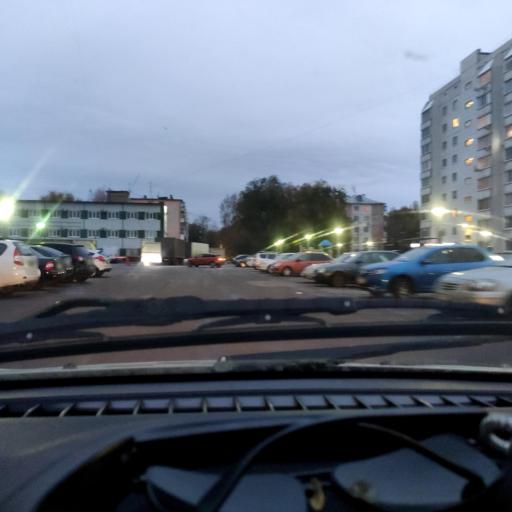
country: RU
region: Samara
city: Tol'yatti
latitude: 53.5197
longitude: 49.4222
